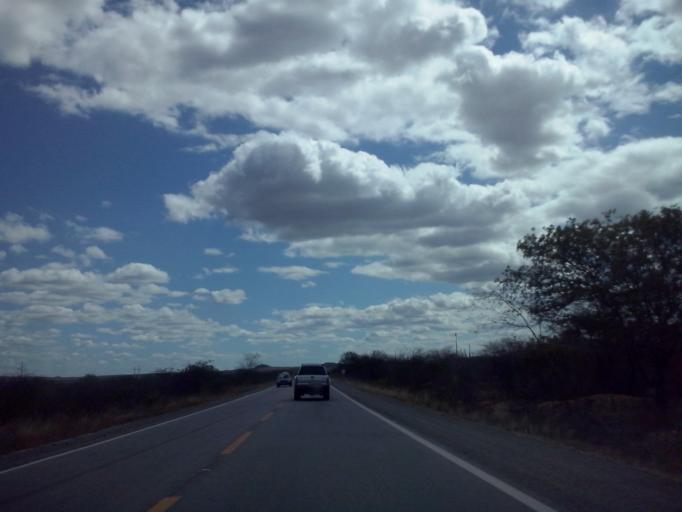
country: BR
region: Paraiba
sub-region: Soledade
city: Soledade
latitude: -7.0385
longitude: -36.4233
